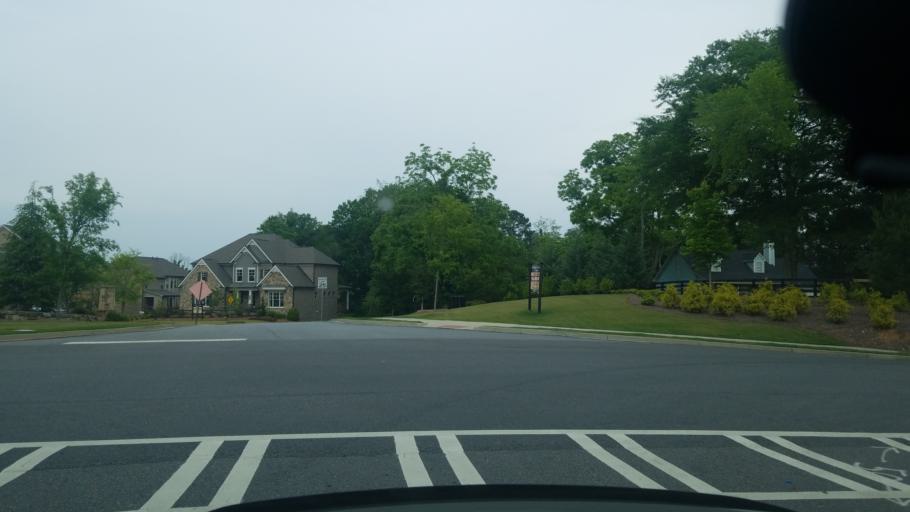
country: US
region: Georgia
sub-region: Gwinnett County
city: Suwanee
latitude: 34.1172
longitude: -84.1283
